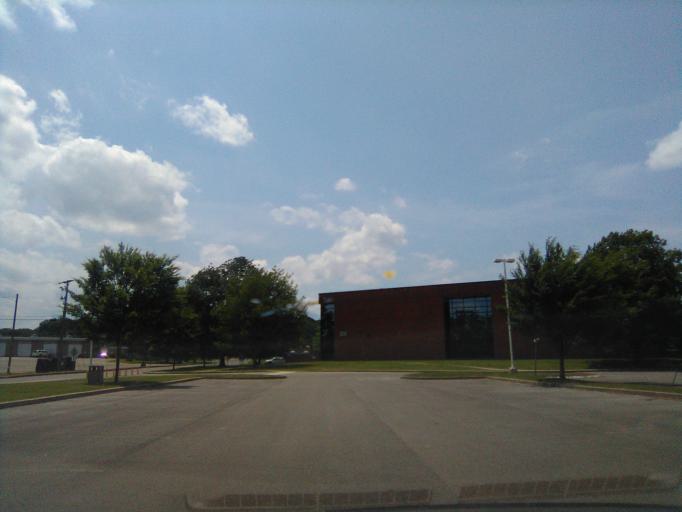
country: US
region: Tennessee
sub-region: Davidson County
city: Belle Meade
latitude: 36.1339
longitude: -86.8545
